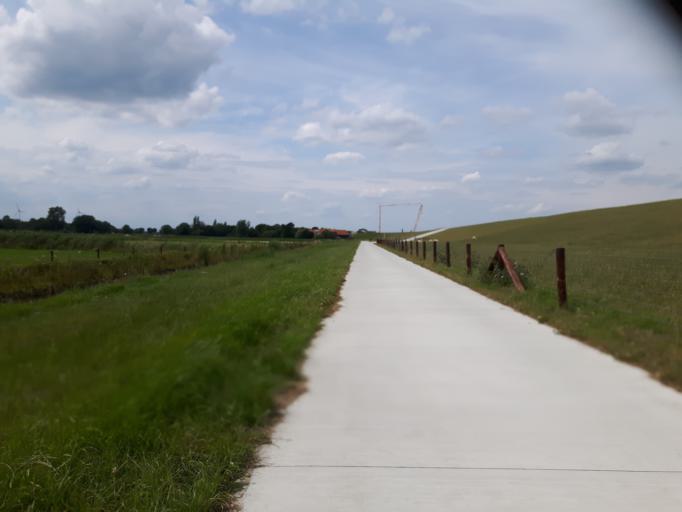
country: DE
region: Lower Saxony
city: Varel
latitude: 53.3907
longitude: 8.2172
